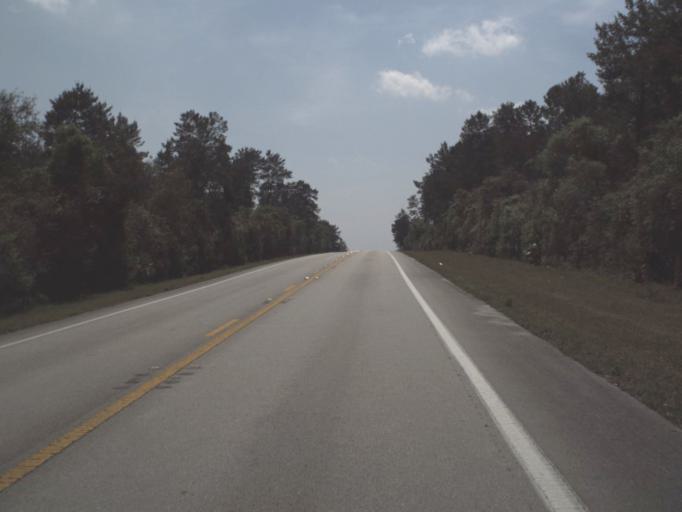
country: US
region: Florida
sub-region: Lake County
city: Astor
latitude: 29.1780
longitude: -81.6487
